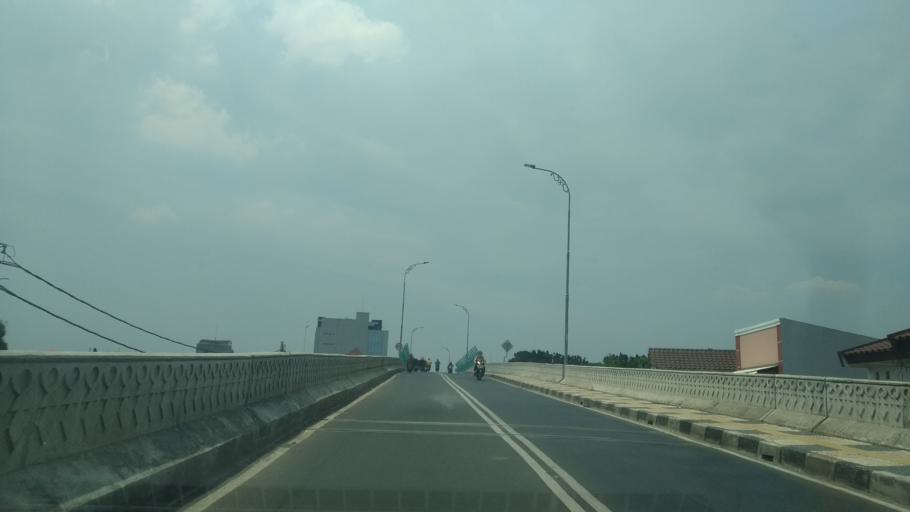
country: ID
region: Banten
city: South Tangerang
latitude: -6.2564
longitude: 106.7621
